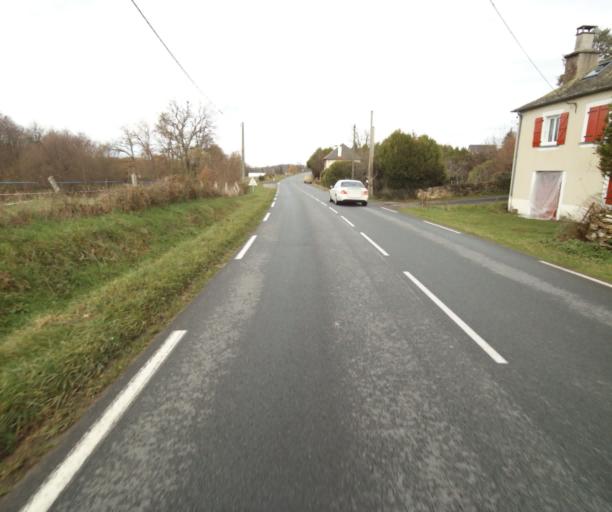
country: FR
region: Limousin
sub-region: Departement de la Correze
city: Saint-Mexant
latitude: 45.2674
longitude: 1.6371
